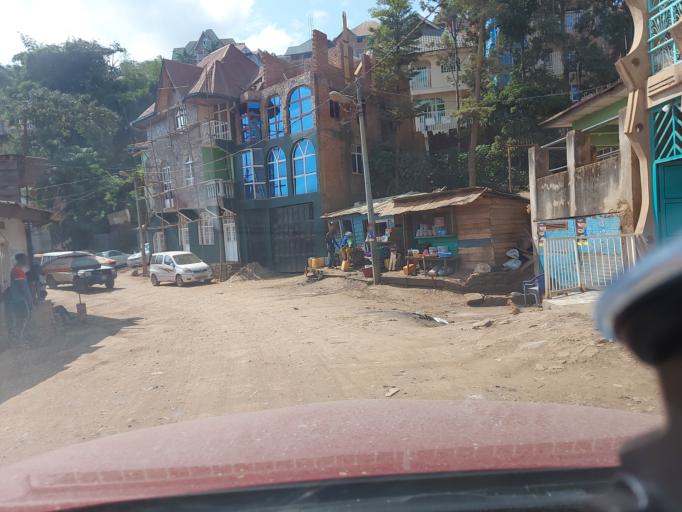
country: CD
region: South Kivu
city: Bukavu
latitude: -2.5001
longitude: 28.8571
